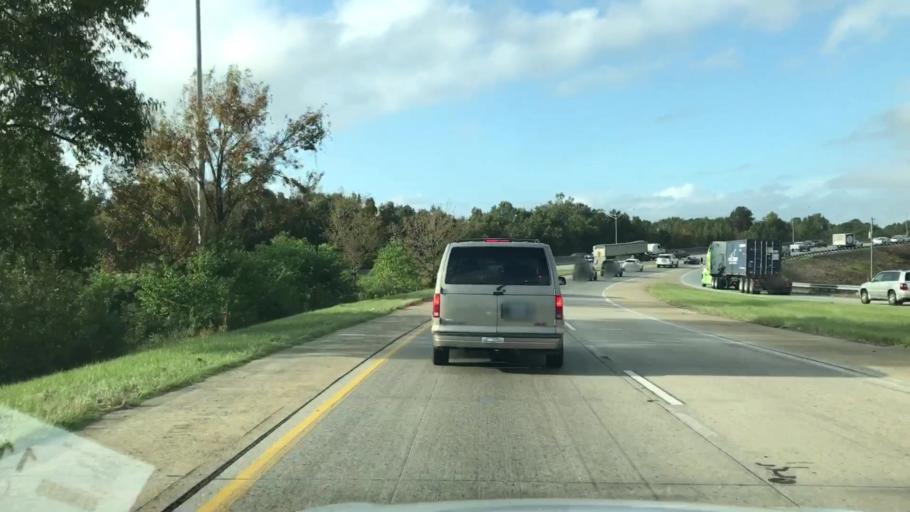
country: US
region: South Carolina
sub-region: Berkeley County
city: Hanahan
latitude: 32.8859
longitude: -80.0190
